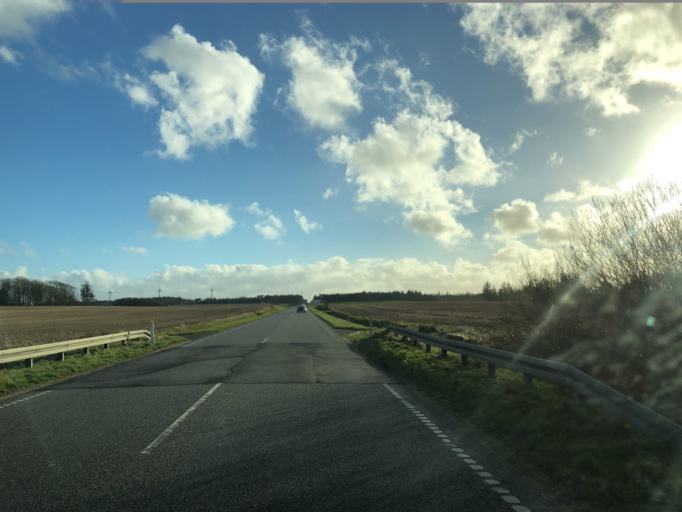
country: DK
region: Central Jutland
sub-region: Herning Kommune
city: Vildbjerg
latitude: 56.1859
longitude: 8.7053
